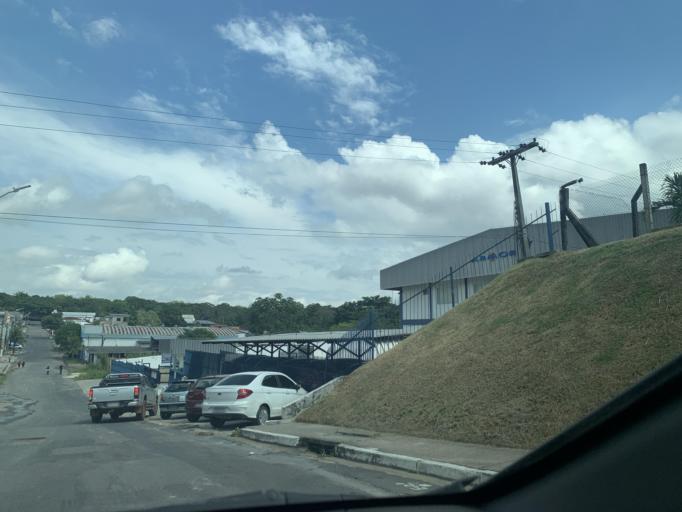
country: BR
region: Amazonas
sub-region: Manaus
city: Manaus
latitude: -3.0926
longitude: -59.9500
